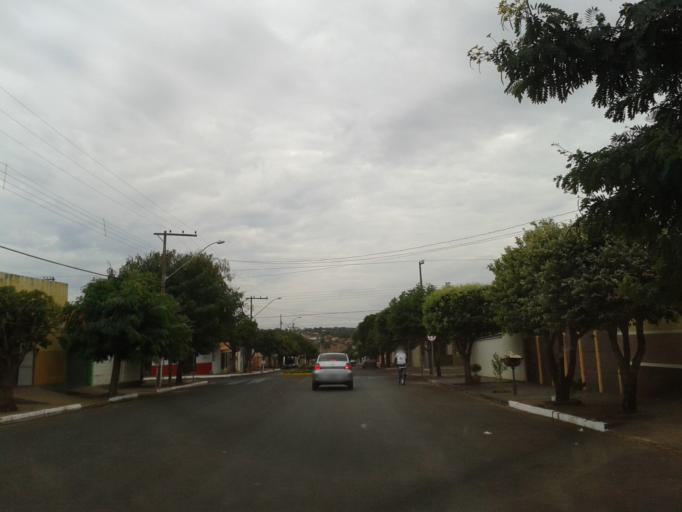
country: BR
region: Minas Gerais
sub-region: Santa Vitoria
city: Santa Vitoria
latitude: -18.8464
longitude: -50.1247
